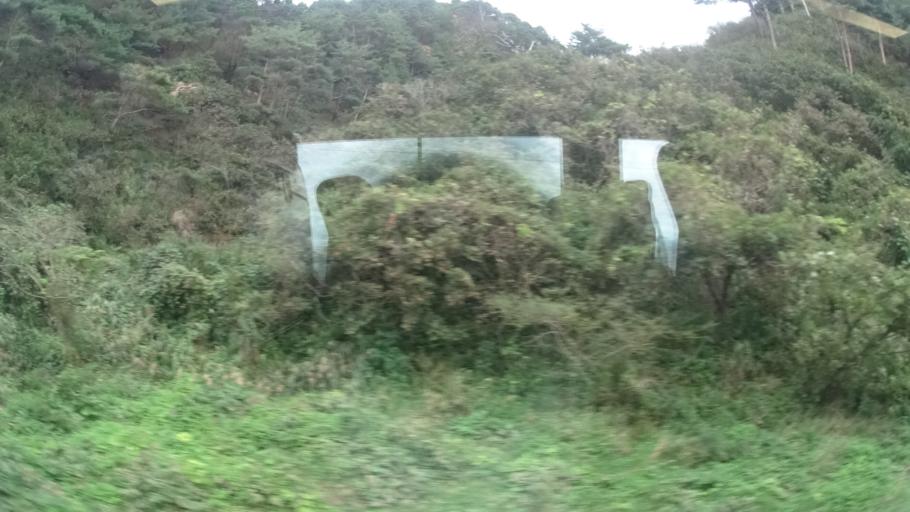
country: JP
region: Niigata
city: Murakami
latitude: 38.4254
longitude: 139.4757
